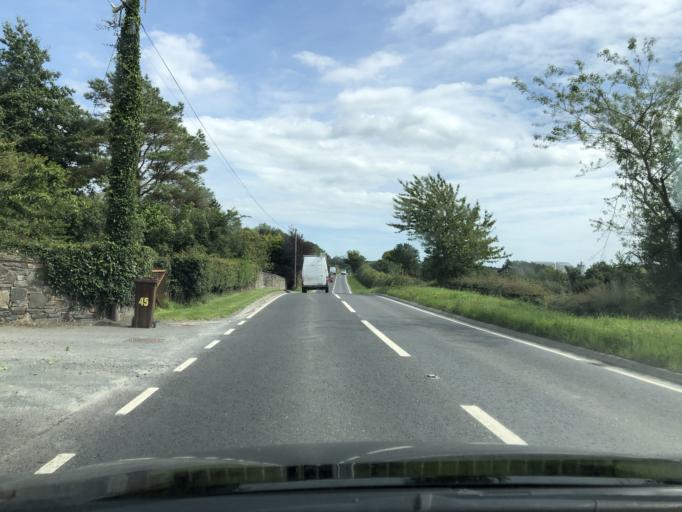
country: GB
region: Northern Ireland
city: Ballynahinch
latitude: 54.4199
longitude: -5.9145
